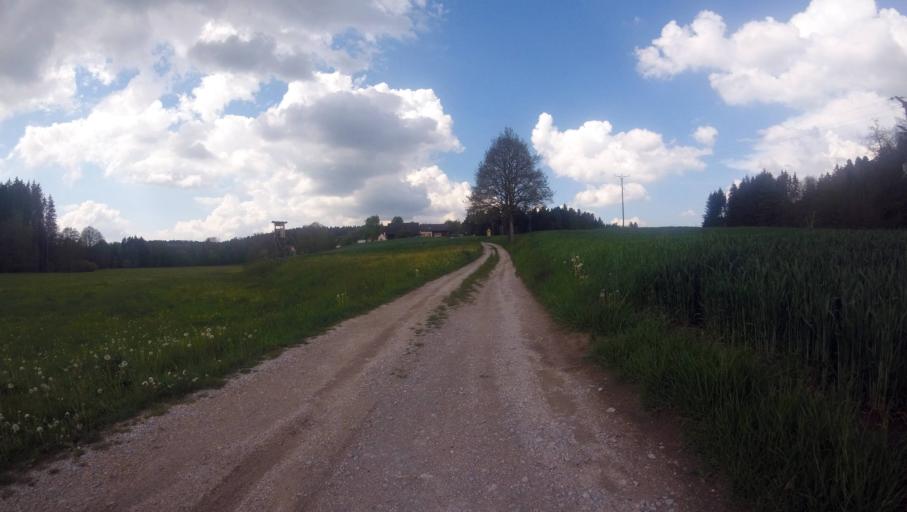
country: DE
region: Baden-Wuerttemberg
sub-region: Regierungsbezirk Stuttgart
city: Spraitbach
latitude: 48.8644
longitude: 9.7497
